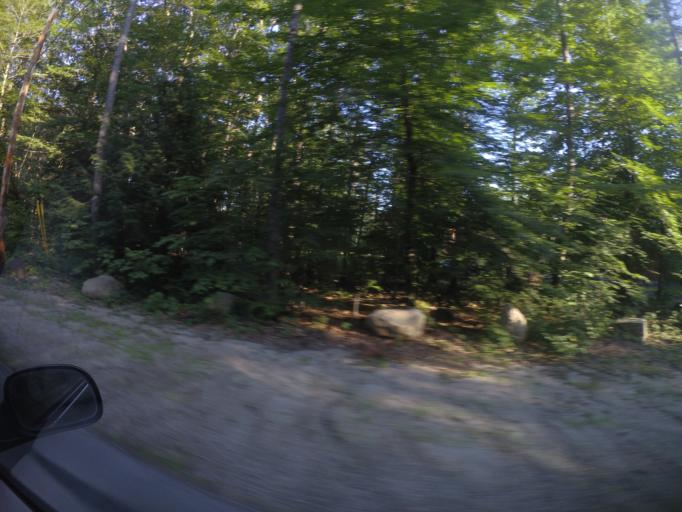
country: US
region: Maine
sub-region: Cumberland County
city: Raymond
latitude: 43.8875
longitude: -70.4190
